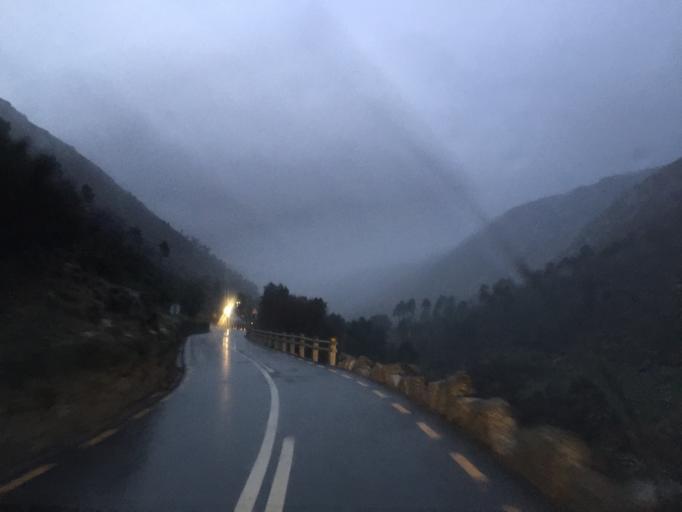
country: PT
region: Guarda
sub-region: Manteigas
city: Manteigas
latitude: 40.3619
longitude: -7.5542
